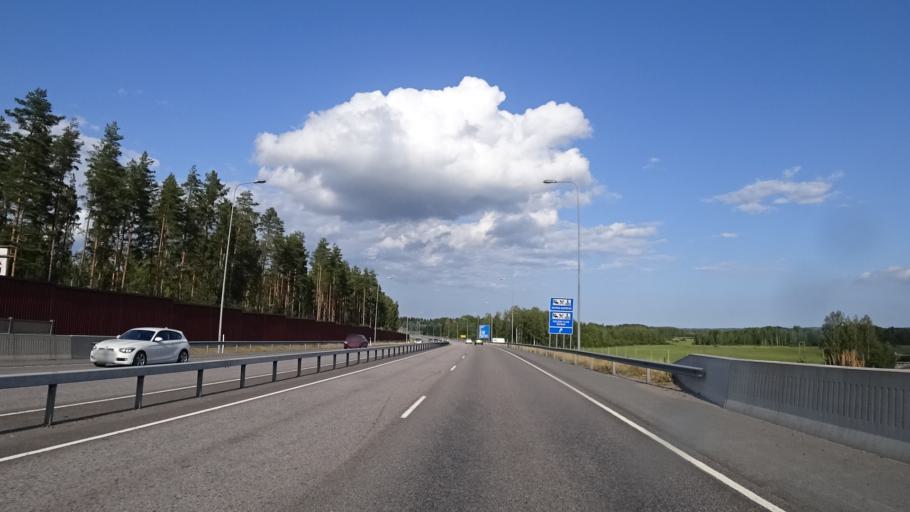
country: FI
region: South Karelia
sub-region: Imatra
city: Imatra
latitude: 61.1658
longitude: 28.6788
